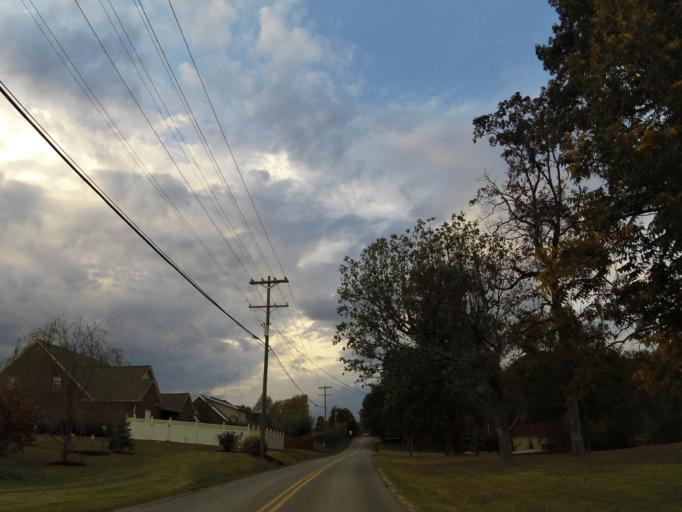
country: US
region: Tennessee
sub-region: Blount County
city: Louisville
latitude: 35.7683
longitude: -84.0273
